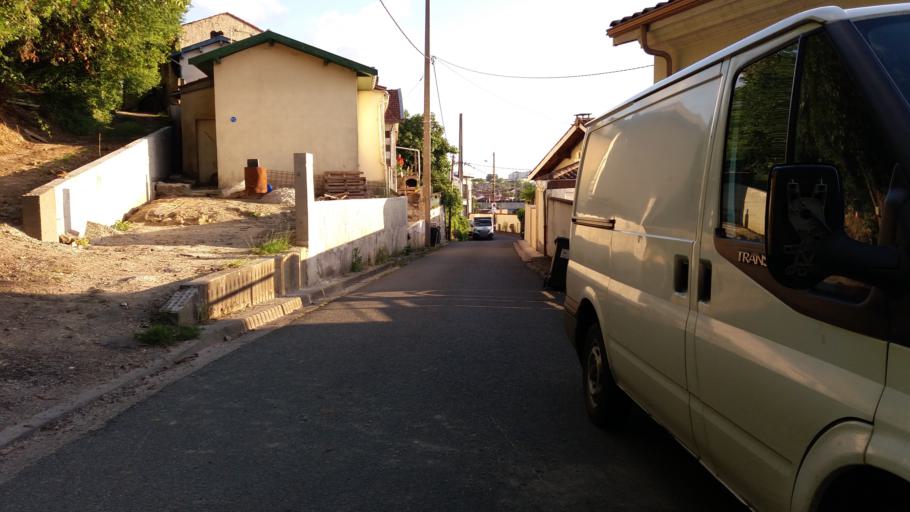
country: FR
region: Aquitaine
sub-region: Departement de la Gironde
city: Cenon
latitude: 44.8535
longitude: -0.5306
